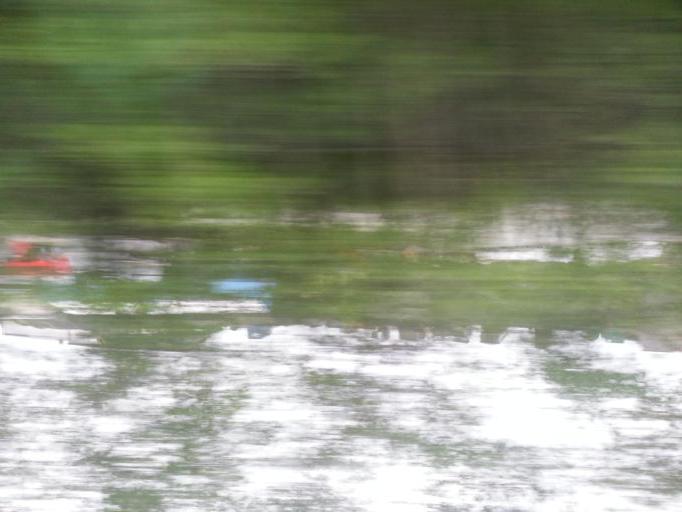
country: NO
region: Sor-Trondelag
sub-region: Melhus
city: Melhus
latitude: 63.3428
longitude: 10.3460
